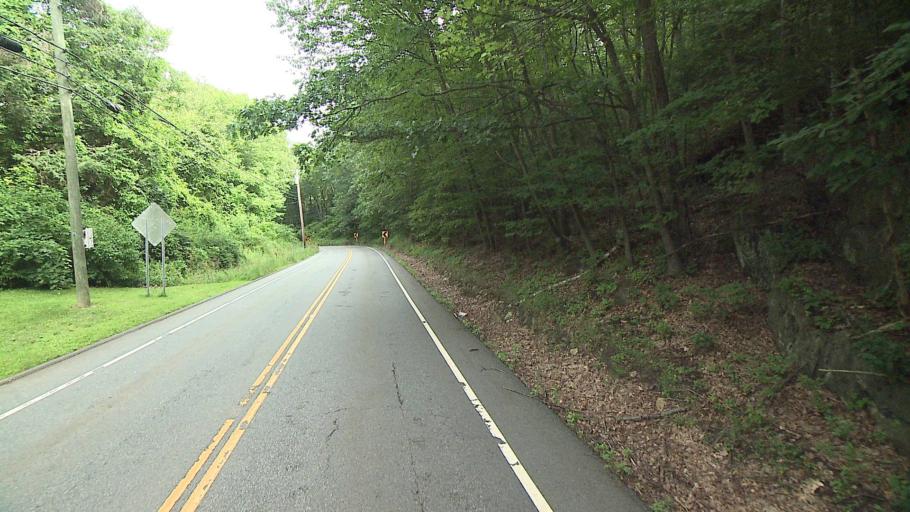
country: US
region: Connecticut
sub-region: Litchfield County
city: Kent
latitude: 41.7198
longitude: -73.4513
